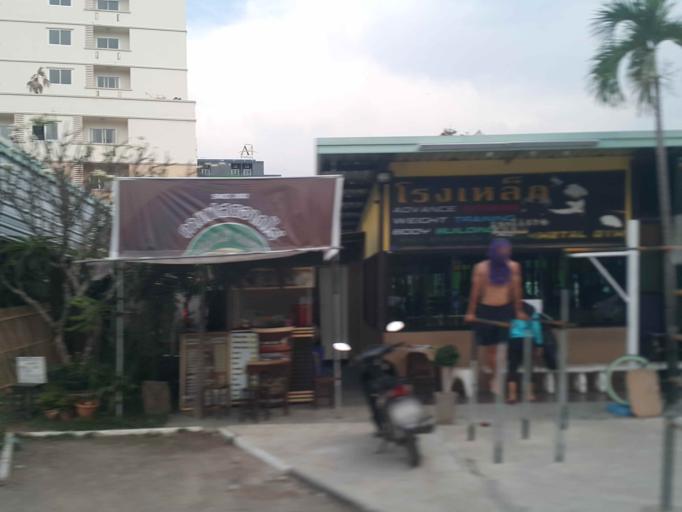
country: TH
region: Chiang Mai
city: Chiang Mai
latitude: 18.7942
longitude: 99.0252
